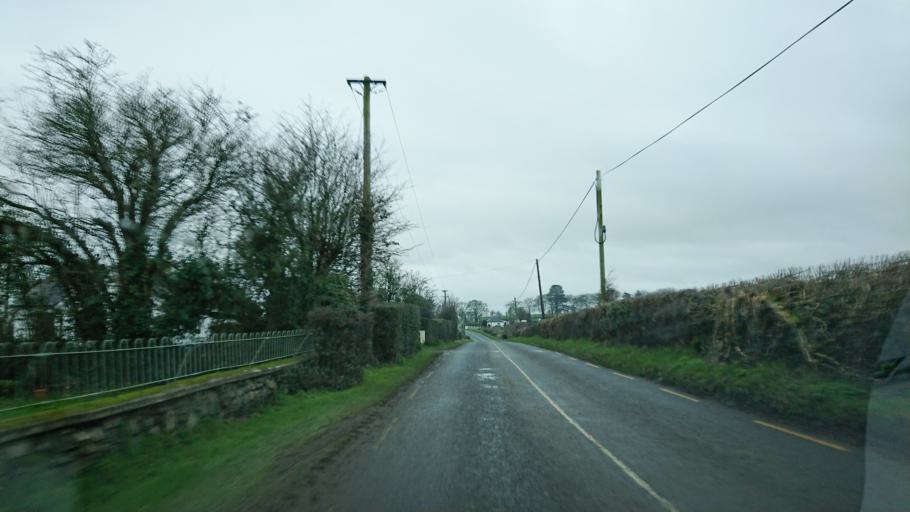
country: IE
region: Leinster
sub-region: Kilkenny
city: Callan
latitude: 52.5286
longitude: -7.2986
